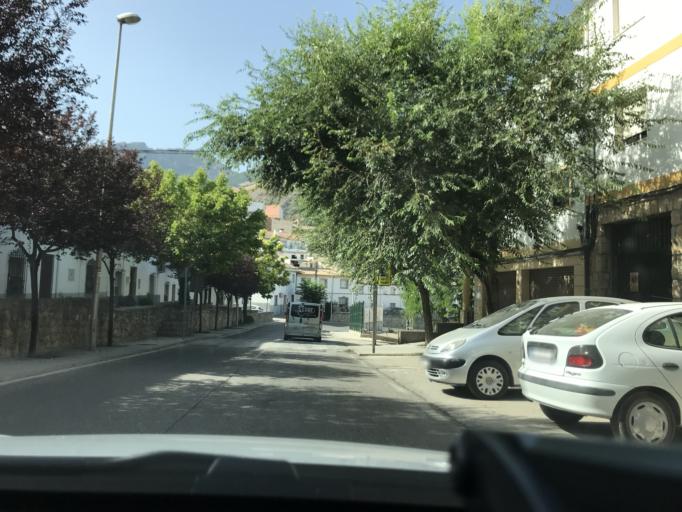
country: ES
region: Andalusia
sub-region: Provincia de Jaen
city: Cazorla
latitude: 37.9180
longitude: -3.0060
